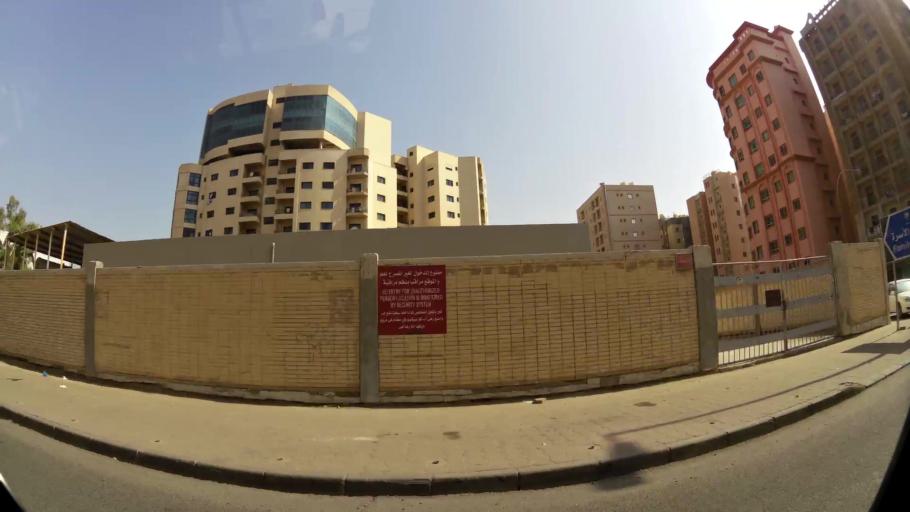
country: KW
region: Muhafazat Hawalli
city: Hawalli
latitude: 29.3383
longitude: 48.0306
